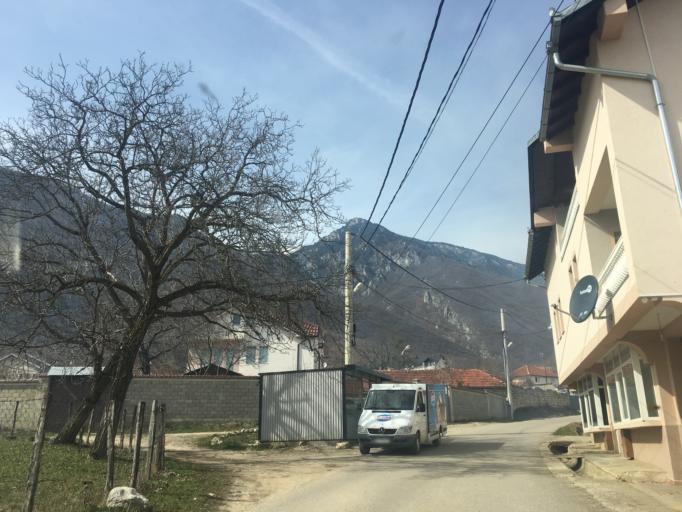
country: XK
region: Gjakova
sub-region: Komuna e Decanit
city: Strellc i Eperm
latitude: 42.5970
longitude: 20.2925
